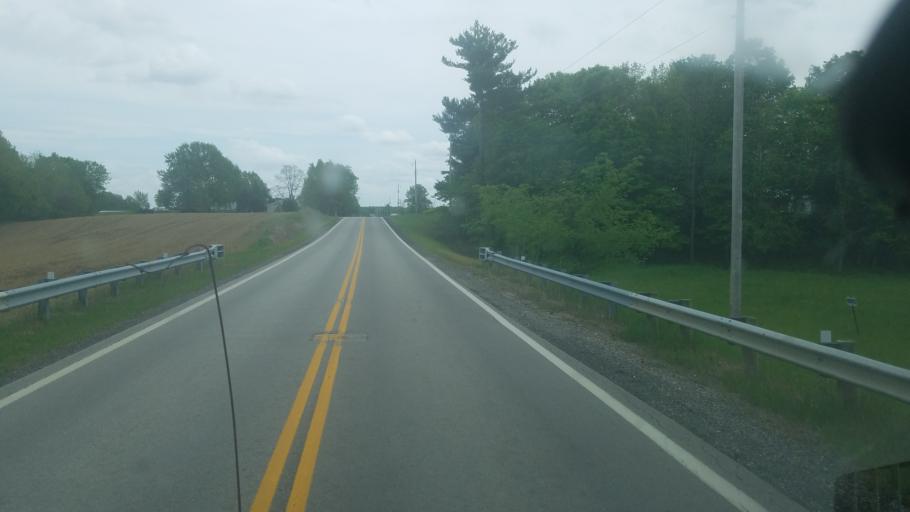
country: US
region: Ohio
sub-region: Crawford County
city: Bucyrus
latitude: 40.9319
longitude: -83.0535
